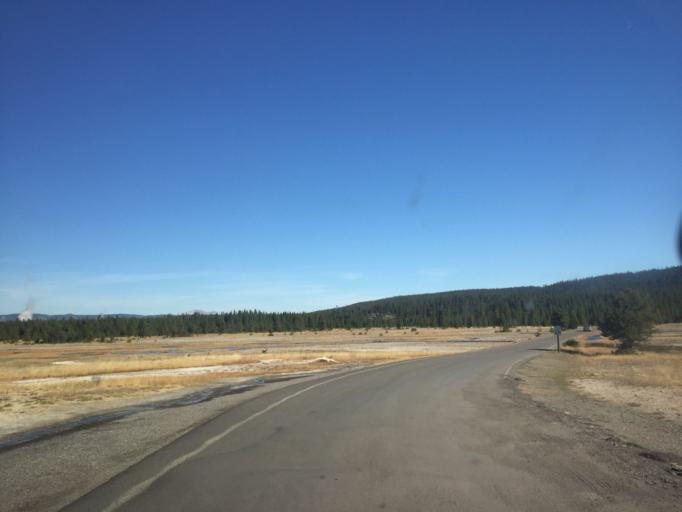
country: US
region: Montana
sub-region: Gallatin County
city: West Yellowstone
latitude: 44.5394
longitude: -110.8023
